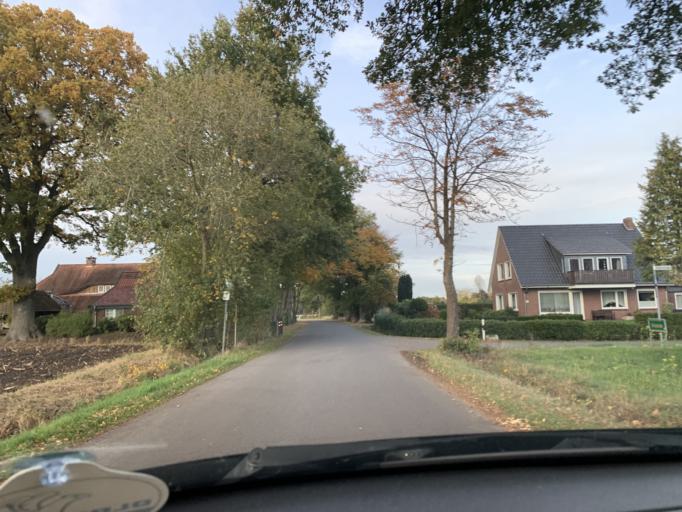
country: DE
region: Lower Saxony
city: Bad Zwischenahn
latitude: 53.2283
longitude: 8.0458
